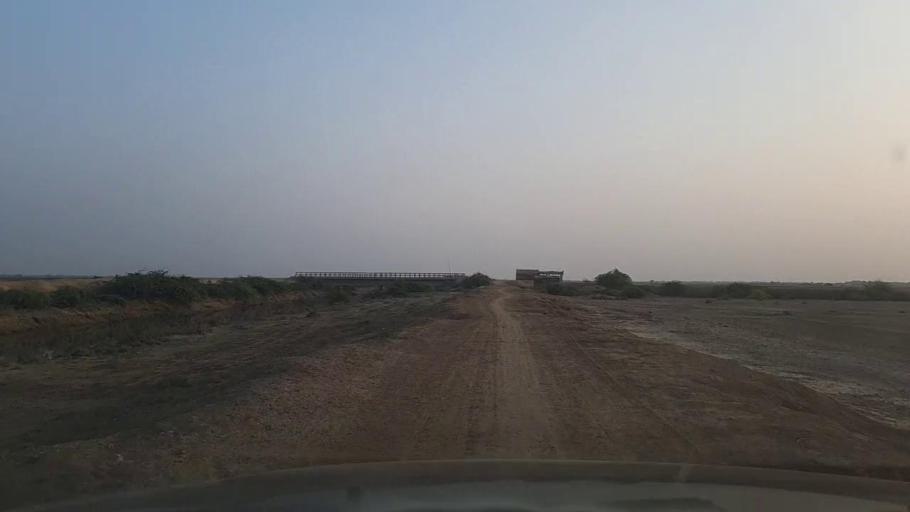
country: PK
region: Sindh
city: Jati
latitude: 24.5311
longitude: 68.4091
